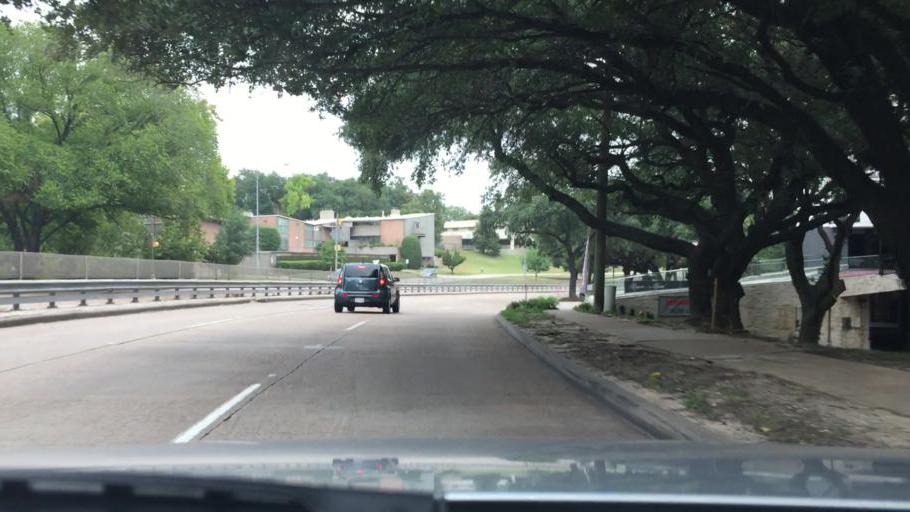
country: US
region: Texas
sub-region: Harris County
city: West University Place
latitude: 29.7610
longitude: -95.4147
